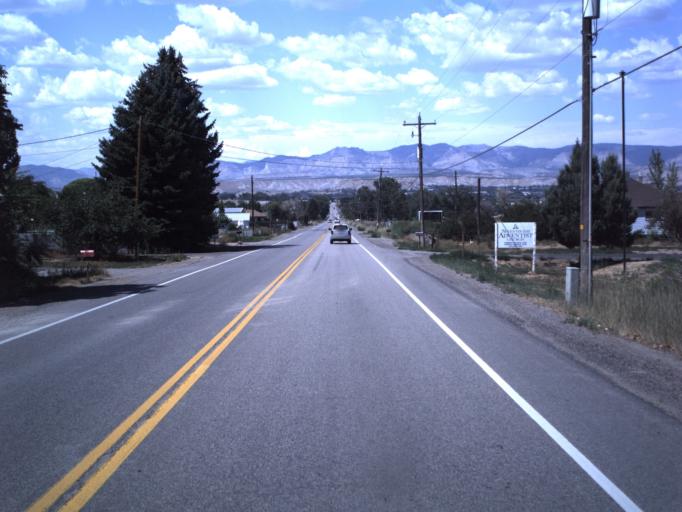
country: US
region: Utah
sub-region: Carbon County
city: Price
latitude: 39.5595
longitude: -110.8158
